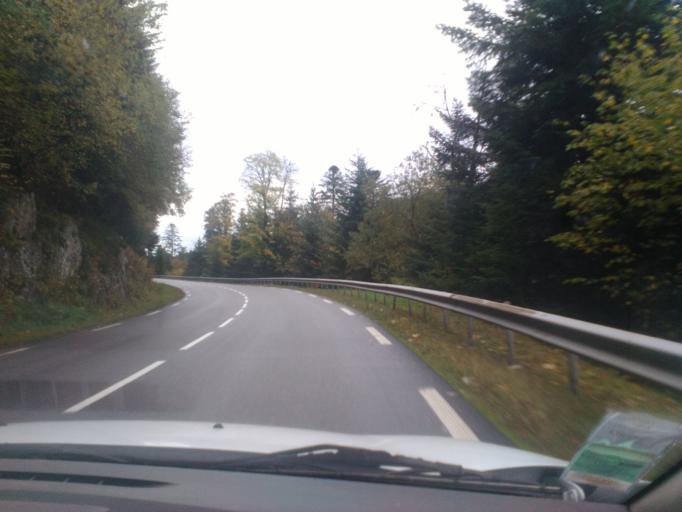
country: FR
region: Lorraine
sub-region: Departement des Vosges
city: Xonrupt-Longemer
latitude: 48.1112
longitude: 6.9098
